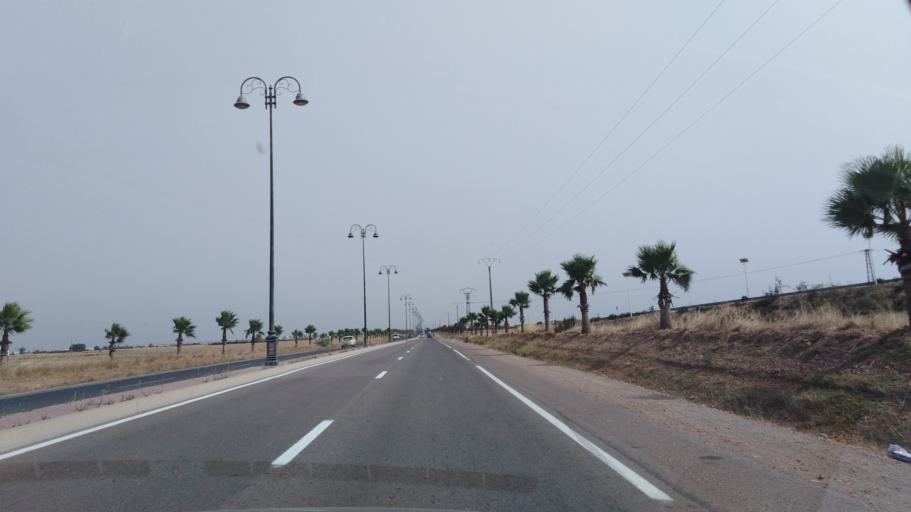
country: MA
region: Chaouia-Ouardigha
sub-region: Settat Province
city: Berrechid
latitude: 33.3057
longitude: -7.6012
